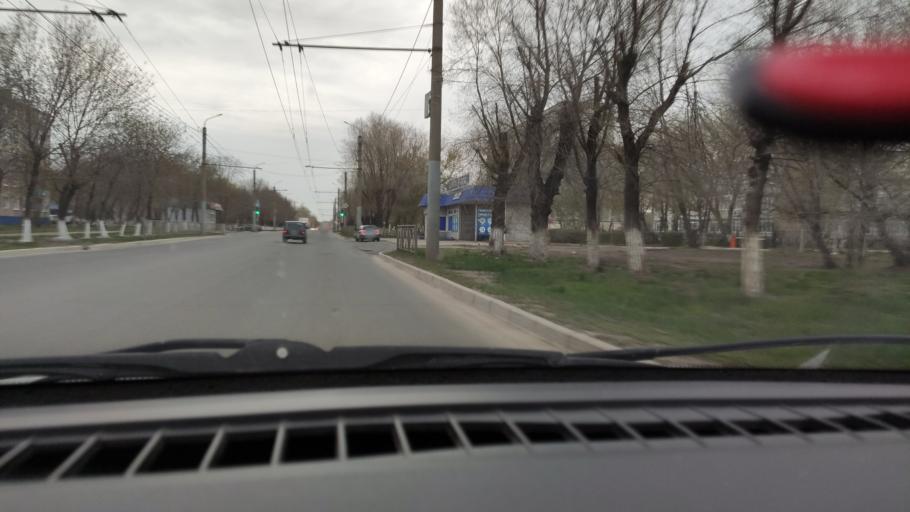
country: RU
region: Orenburg
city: Orenburg
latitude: 51.8421
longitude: 55.1287
